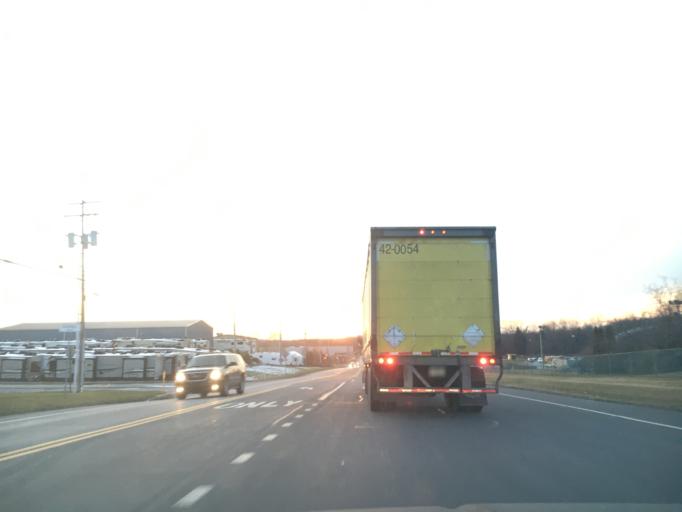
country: US
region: Pennsylvania
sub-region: Northampton County
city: Wind Gap
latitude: 40.8316
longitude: -75.3035
